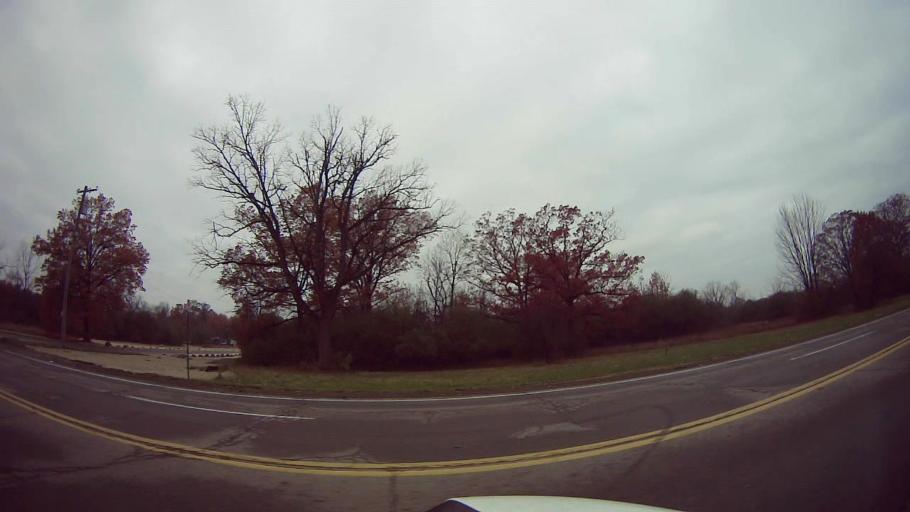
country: US
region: Michigan
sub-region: Wayne County
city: Dearborn Heights
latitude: 42.3504
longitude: -83.2544
